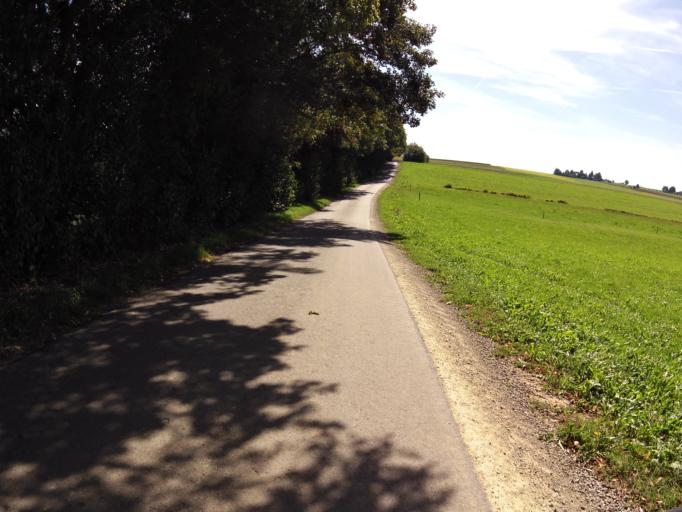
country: DE
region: Baden-Wuerttemberg
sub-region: Freiburg Region
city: Donaueschingen
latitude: 47.9895
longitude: 8.5051
